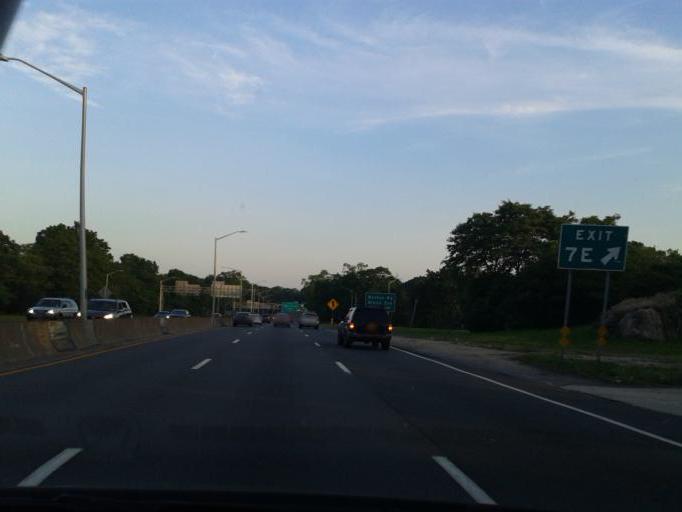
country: US
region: New York
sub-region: Bronx
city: The Bronx
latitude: 40.8555
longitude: -73.8723
